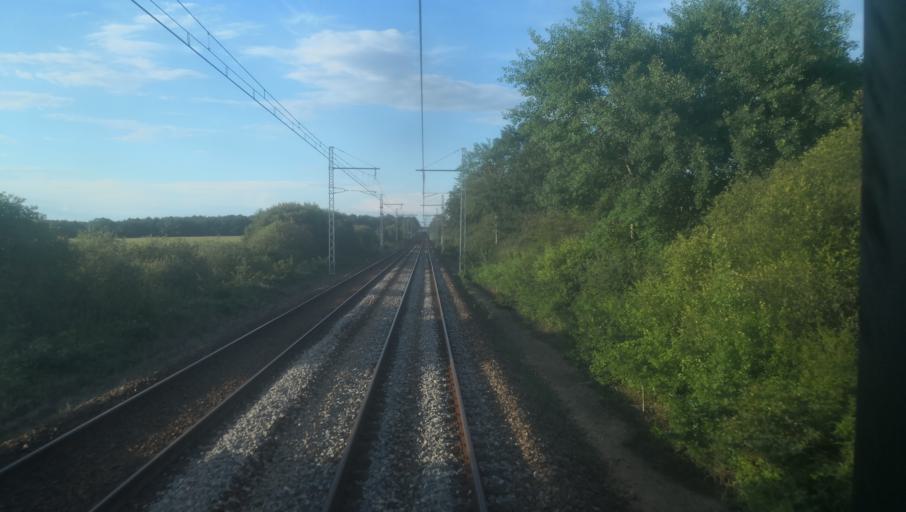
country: FR
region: Centre
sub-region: Departement de l'Indre
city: Luant
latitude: 46.7087
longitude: 1.5726
